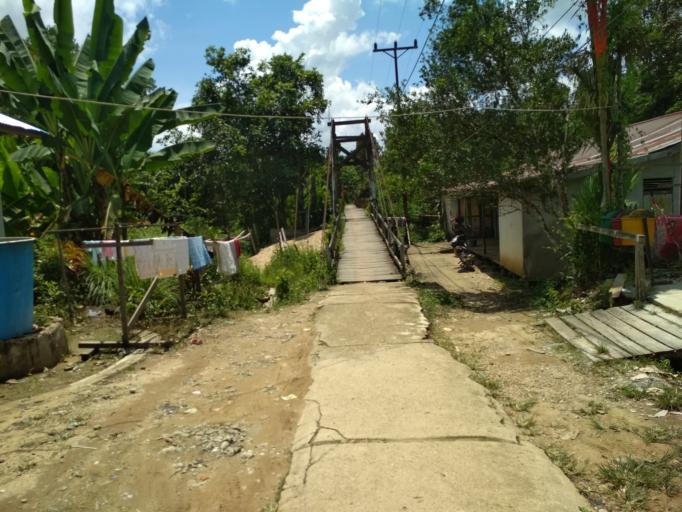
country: ID
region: West Kalimantan
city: Bengkayang
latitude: 0.7533
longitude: 110.1009
